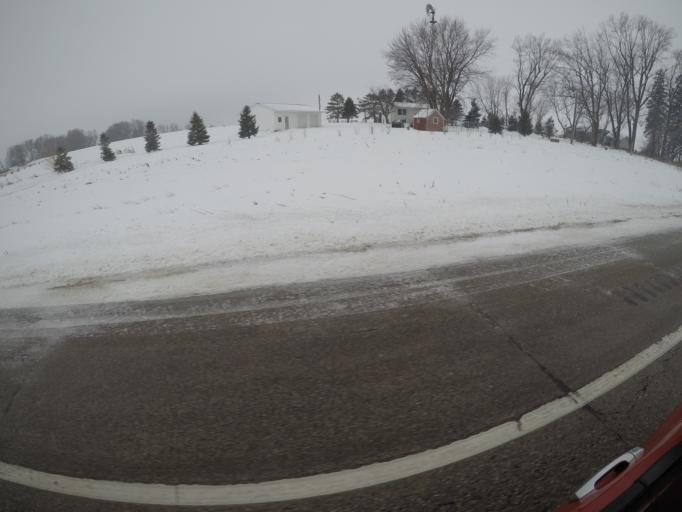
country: US
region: Minnesota
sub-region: Goodhue County
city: Wanamingo
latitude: 44.3367
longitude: -92.7478
